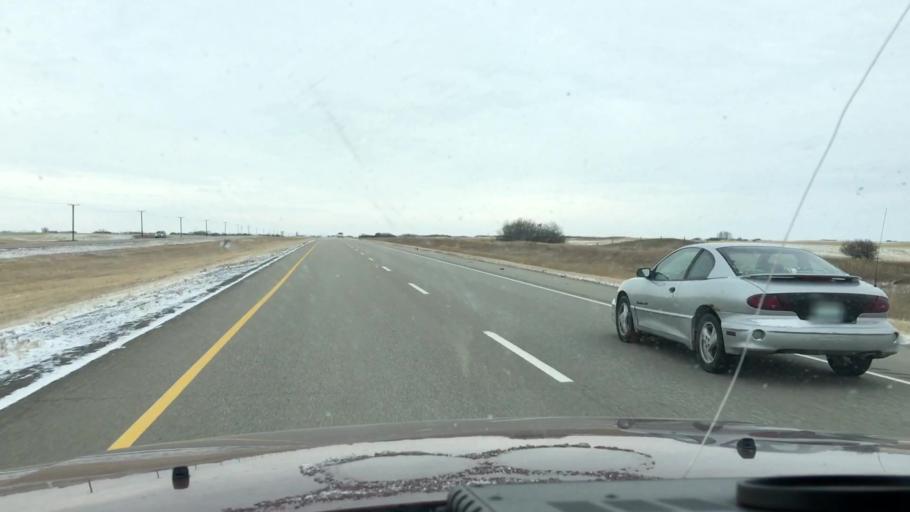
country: CA
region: Saskatchewan
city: Watrous
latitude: 51.4056
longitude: -106.1813
